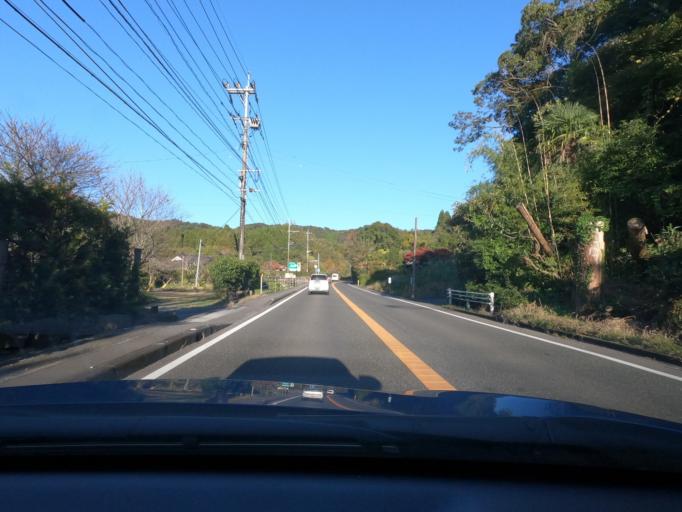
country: JP
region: Kagoshima
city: Satsumasendai
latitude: 31.8504
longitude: 130.2632
